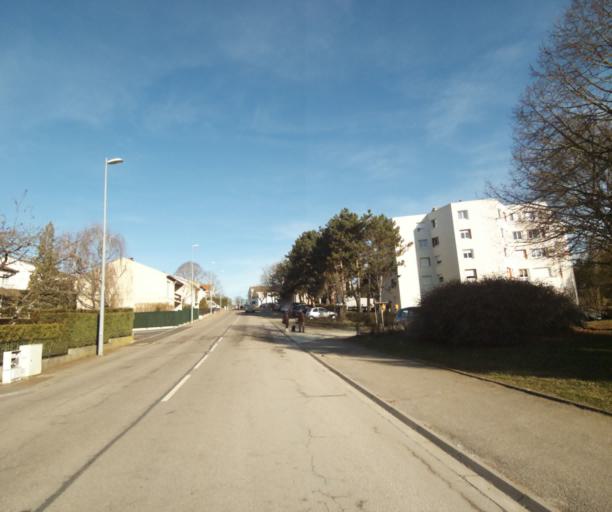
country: FR
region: Lorraine
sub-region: Departement de Meurthe-et-Moselle
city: Chavigny
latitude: 48.6553
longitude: 6.1132
